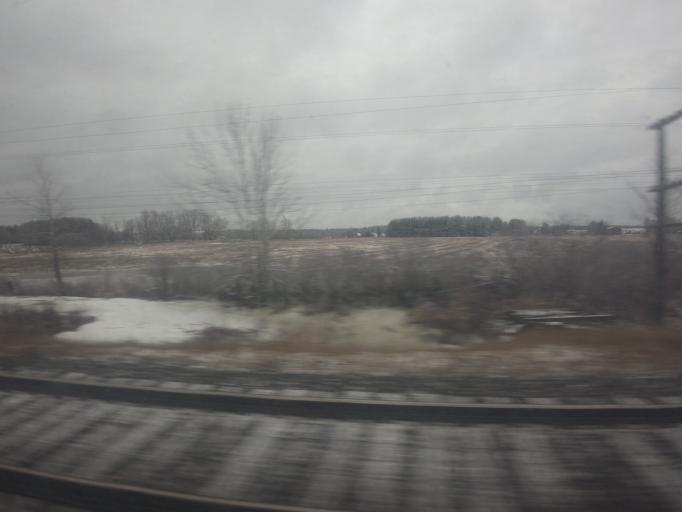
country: CA
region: Ontario
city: Gananoque
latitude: 44.3887
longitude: -76.0507
